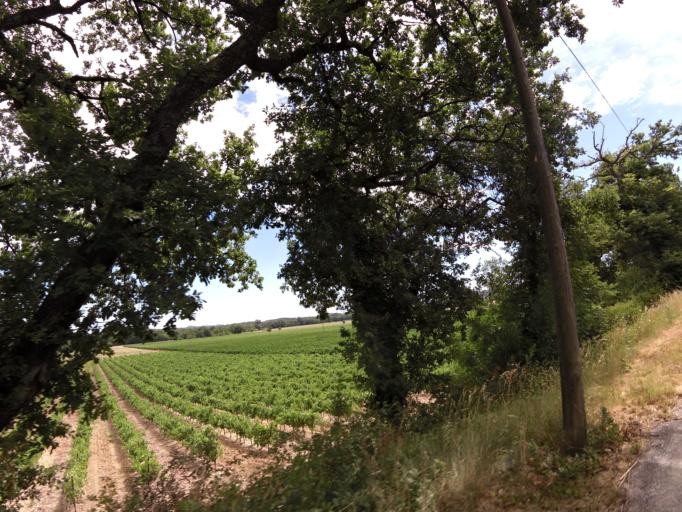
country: FR
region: Languedoc-Roussillon
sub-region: Departement du Gard
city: Quissac
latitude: 43.8912
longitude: 4.0016
